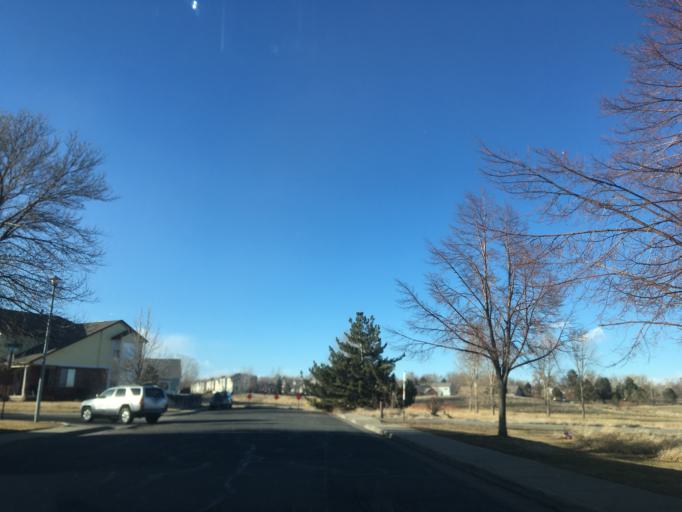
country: US
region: Colorado
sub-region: Adams County
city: Northglenn
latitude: 39.9255
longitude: -104.9551
